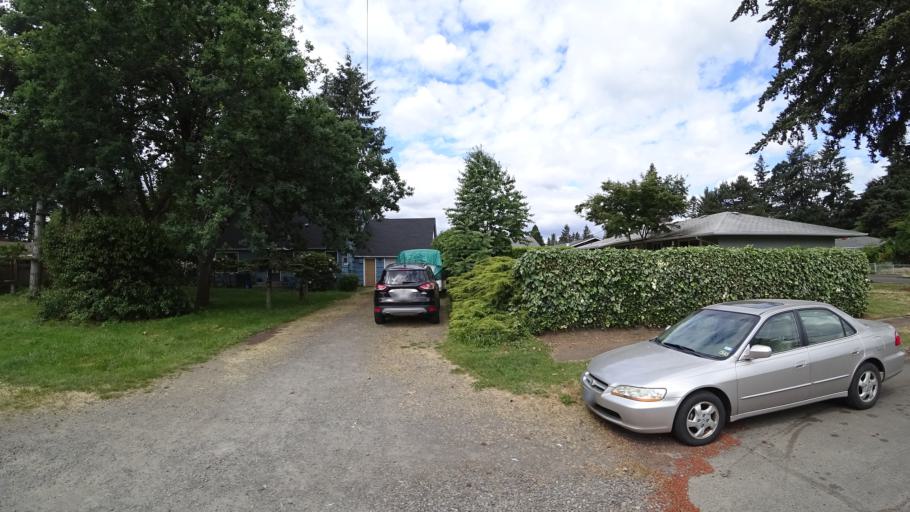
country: US
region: Oregon
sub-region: Multnomah County
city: Lents
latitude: 45.4920
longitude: -122.5275
